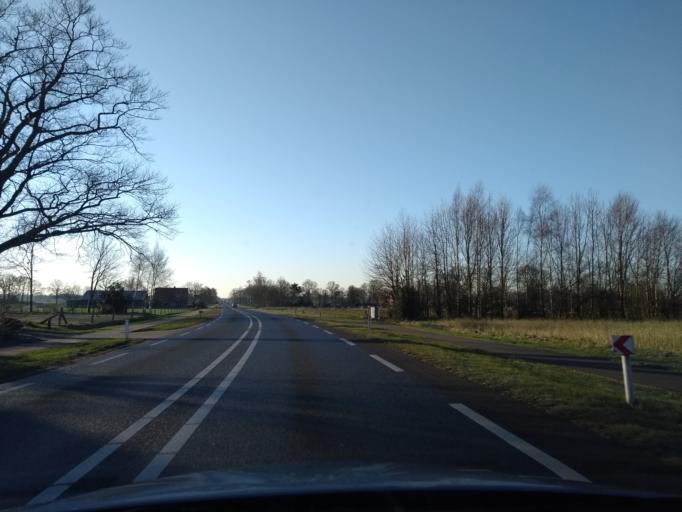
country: NL
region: Overijssel
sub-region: Gemeente Haaksbergen
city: Haaksbergen
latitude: 52.1920
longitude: 6.7356
